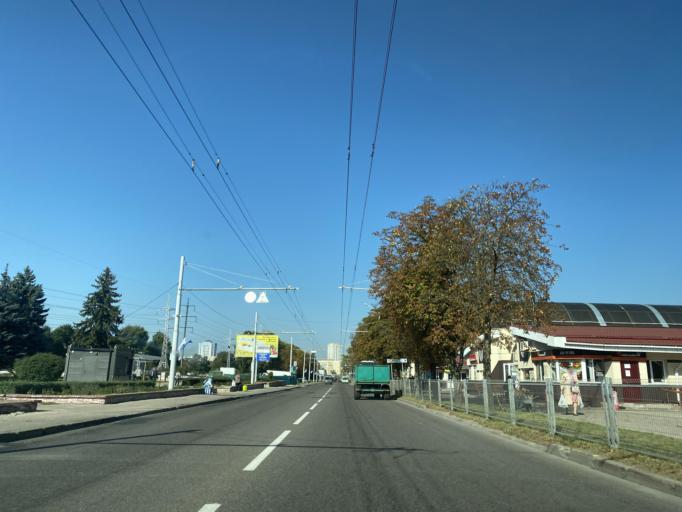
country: BY
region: Minsk
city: Borovlyany
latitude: 53.9464
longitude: 27.6291
